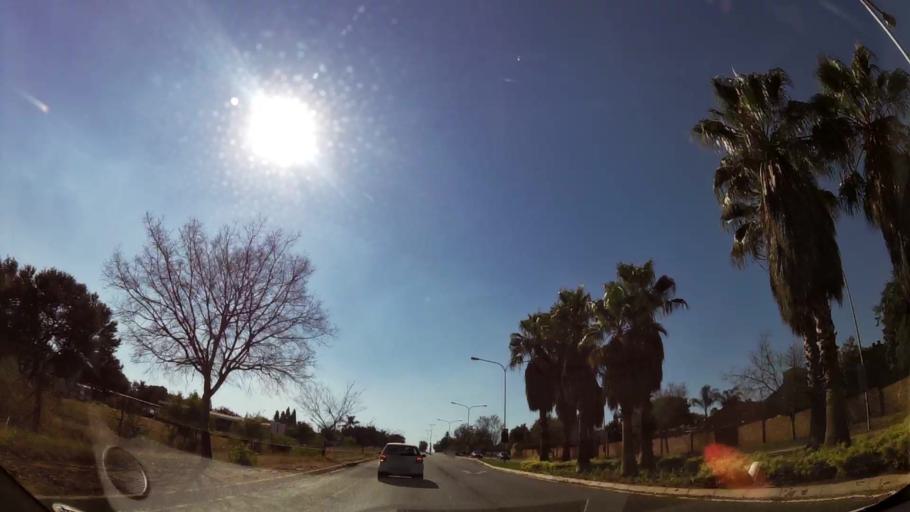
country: ZA
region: Gauteng
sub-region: City of Tshwane Metropolitan Municipality
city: Centurion
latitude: -25.8474
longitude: 28.1999
